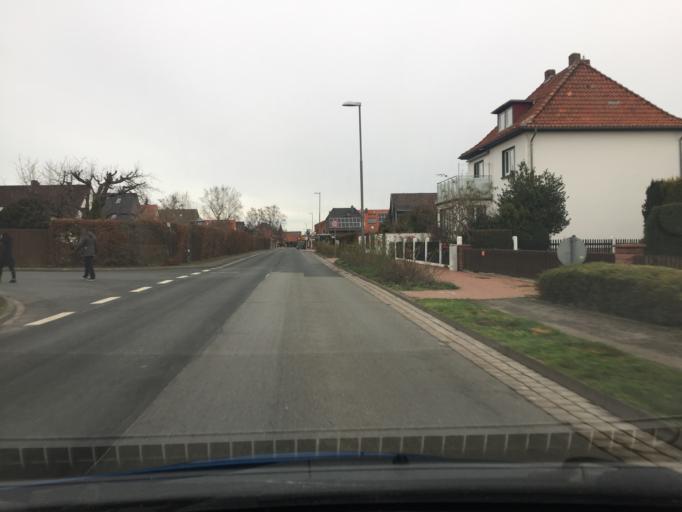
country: DE
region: Lower Saxony
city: Pattensen
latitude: 52.2872
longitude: 9.7664
